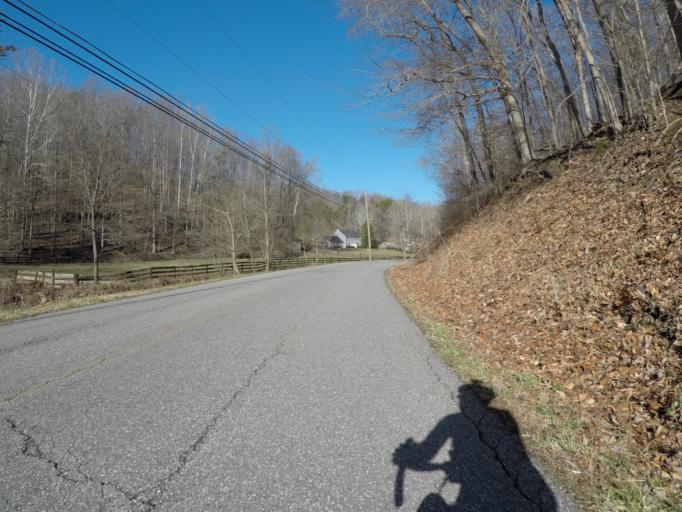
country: US
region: Kentucky
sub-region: Boyd County
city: Catlettsburg
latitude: 38.4227
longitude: -82.6380
